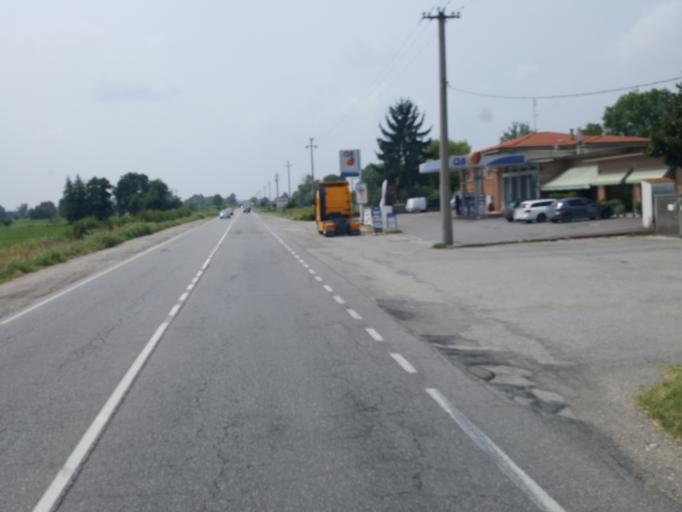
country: IT
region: Lombardy
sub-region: Citta metropolitana di Milano
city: Truccazzano
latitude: 45.4821
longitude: 9.4667
